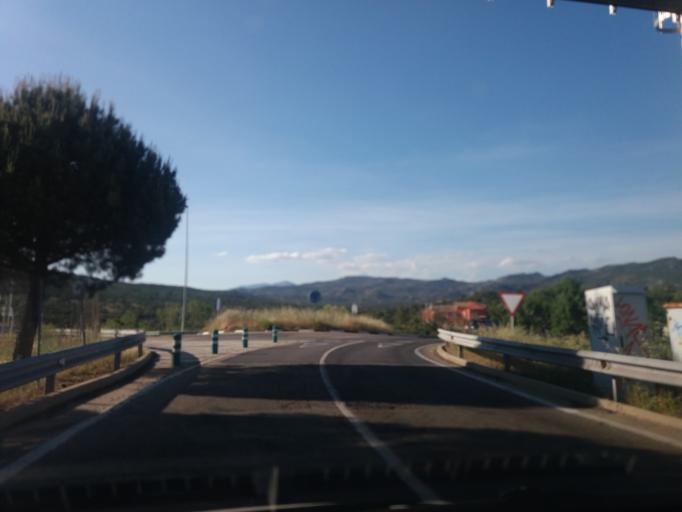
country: ES
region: Madrid
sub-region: Provincia de Madrid
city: Torrelodones
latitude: 40.5948
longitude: -3.9522
